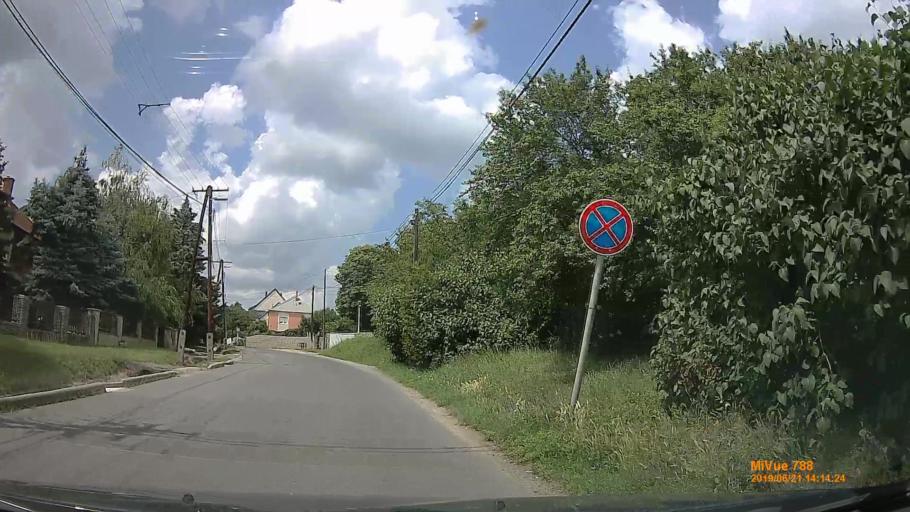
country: HU
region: Baranya
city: Pecs
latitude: 46.0793
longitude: 18.1866
